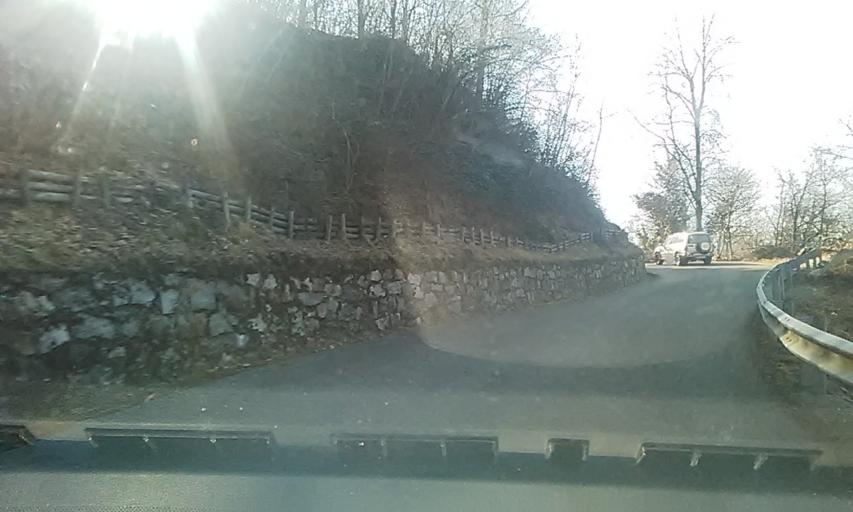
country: IT
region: Piedmont
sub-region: Provincia di Vercelli
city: Quarona
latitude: 45.7610
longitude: 8.2784
